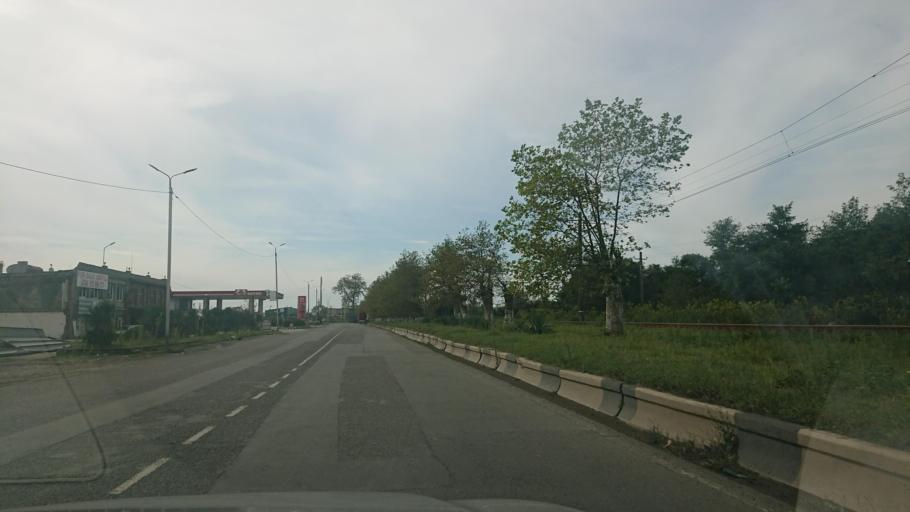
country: GE
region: Samegrelo and Zemo Svaneti
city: P'ot'i
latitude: 42.1707
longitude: 41.6755
